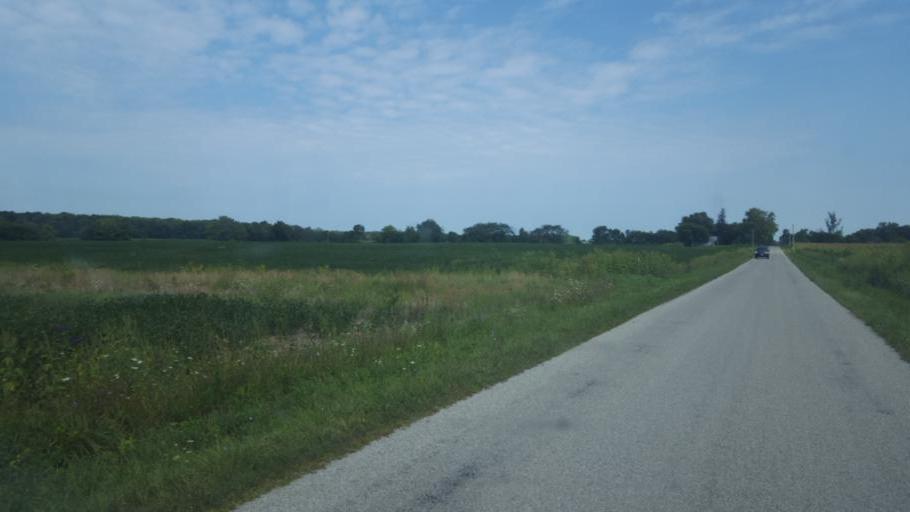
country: US
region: Ohio
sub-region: Delaware County
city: Ashley
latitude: 40.4606
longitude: -83.0480
